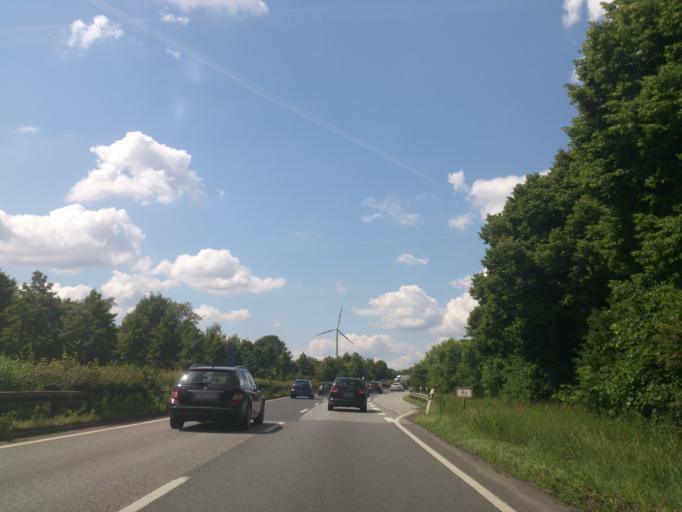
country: DE
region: Lower Saxony
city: Auf der Horst
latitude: 52.4151
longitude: 9.6411
